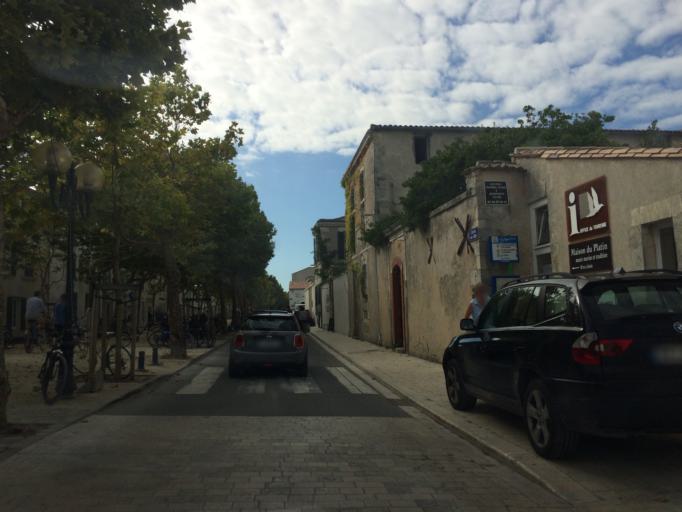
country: FR
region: Poitou-Charentes
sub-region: Departement de la Charente-Maritime
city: La Flotte
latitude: 46.1881
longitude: -1.3242
